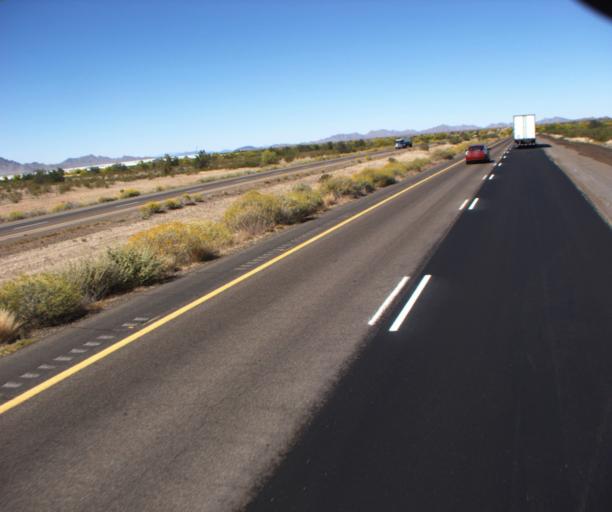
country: US
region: Arizona
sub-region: Maricopa County
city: Gila Bend
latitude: 33.0672
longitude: -112.6454
